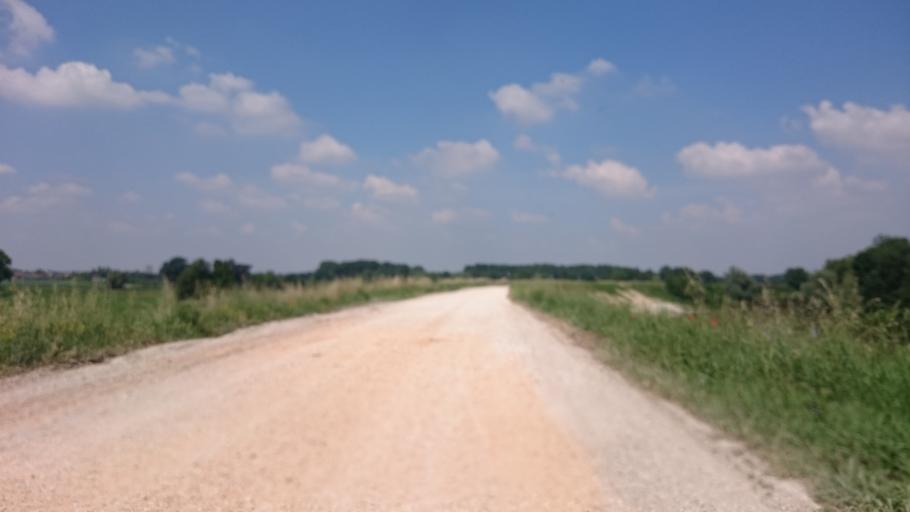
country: IT
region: Lombardy
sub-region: Provincia di Mantova
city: Roncoferraro
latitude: 45.0927
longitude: 10.9315
